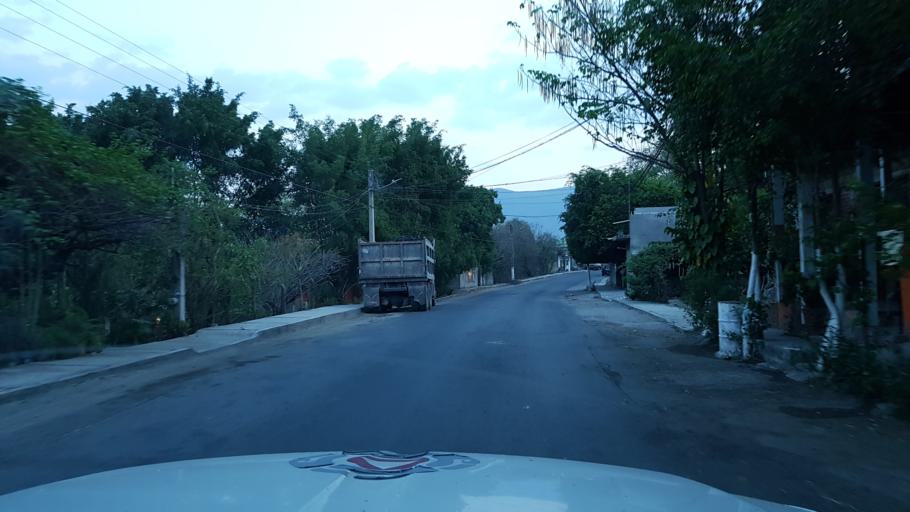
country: MX
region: Morelos
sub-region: Tlaltizapan de Zapata
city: Colonia Palo Prieto (Chipitongo)
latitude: 18.6942
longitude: -99.1135
